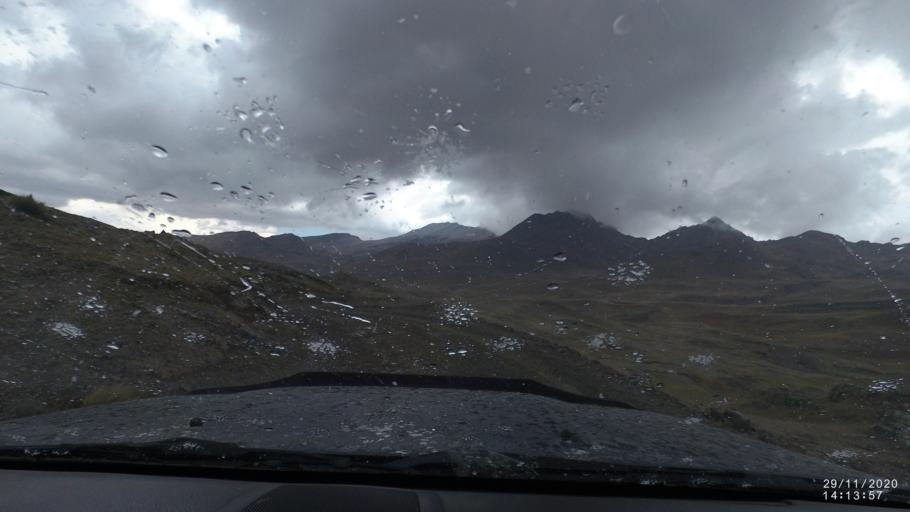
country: BO
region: Cochabamba
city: Sipe Sipe
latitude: -17.2433
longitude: -66.3947
